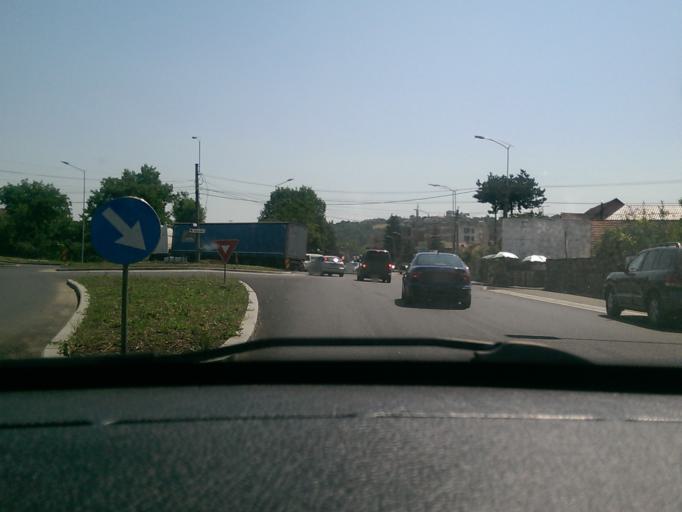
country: RO
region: Cluj
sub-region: Comuna Baciu
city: Baciu
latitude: 46.7838
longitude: 23.5571
